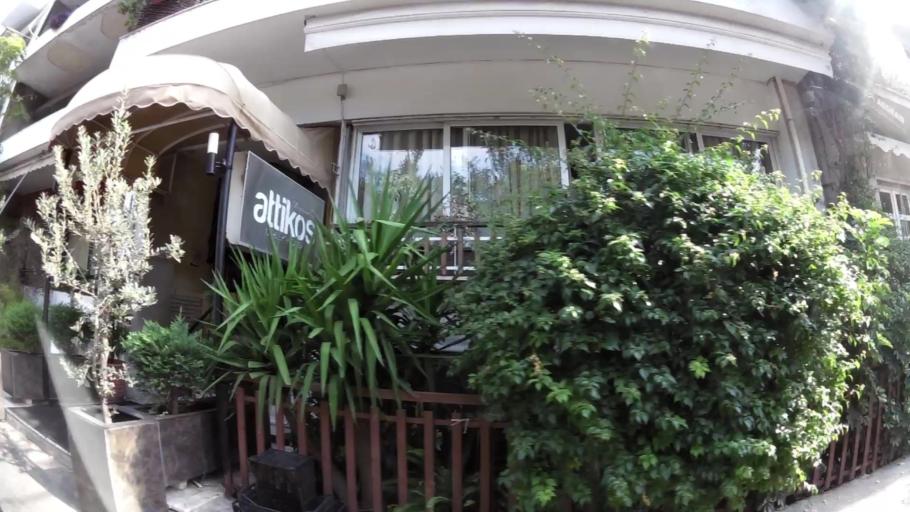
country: GR
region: Attica
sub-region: Nomarchia Athinas
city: Athens
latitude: 37.9691
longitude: 23.7236
